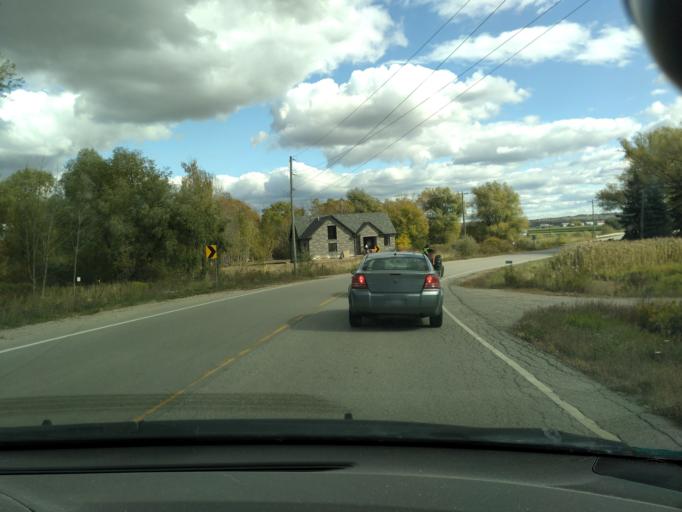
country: CA
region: Ontario
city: Bradford West Gwillimbury
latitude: 44.0852
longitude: -79.5792
